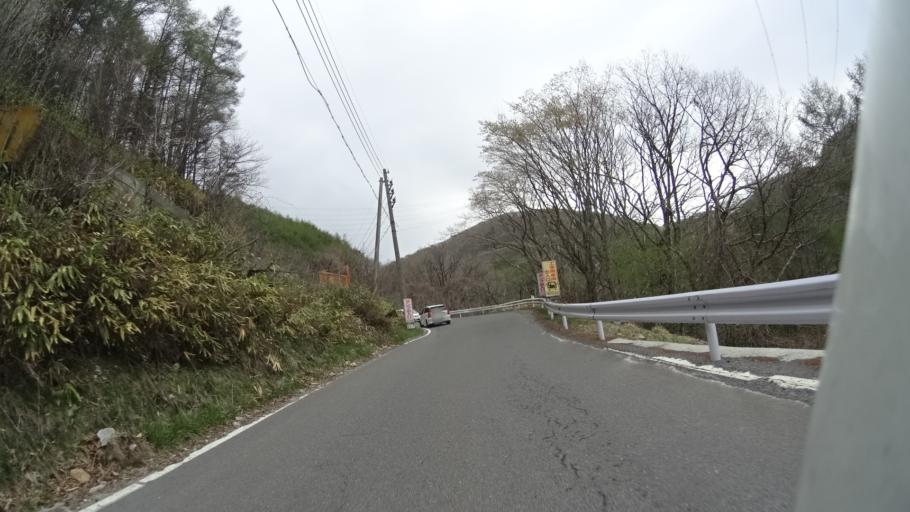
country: JP
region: Nagano
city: Suwa
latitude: 36.1392
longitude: 138.1429
